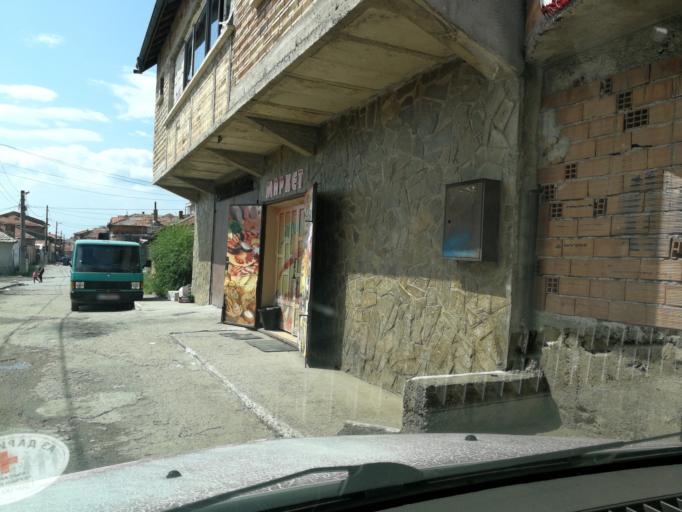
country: BG
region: Stara Zagora
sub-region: Obshtina Stara Zagora
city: Stara Zagora
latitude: 42.4323
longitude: 25.6070
